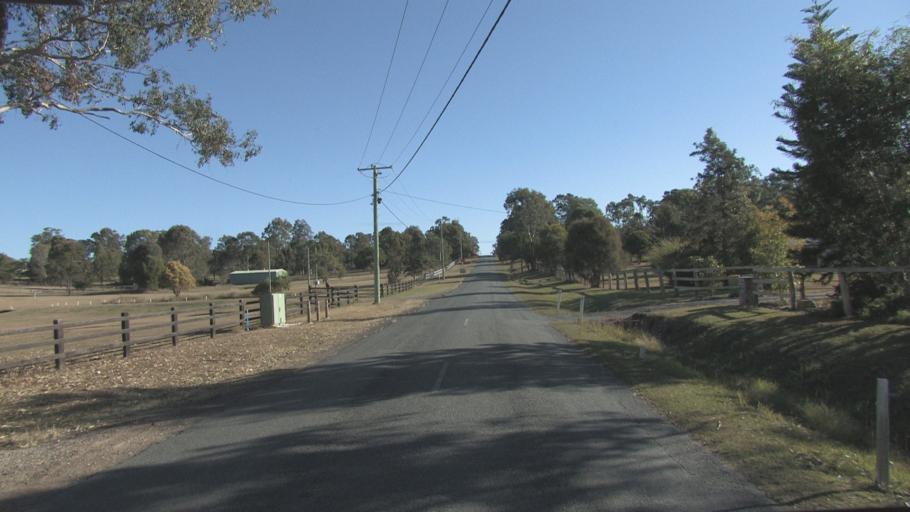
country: AU
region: Queensland
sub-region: Logan
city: Cedar Vale
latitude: -27.8306
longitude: 153.0085
